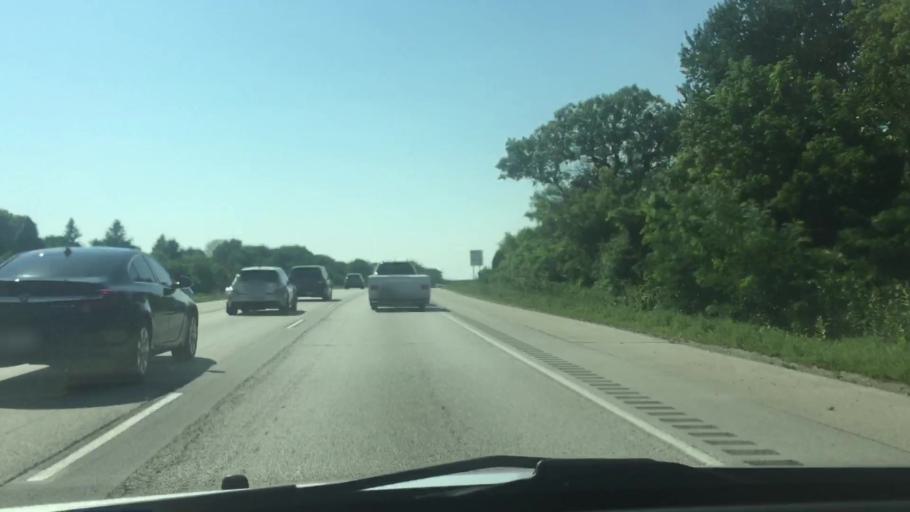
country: US
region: Wisconsin
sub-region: Waukesha County
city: Delafield
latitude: 43.0542
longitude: -88.4156
